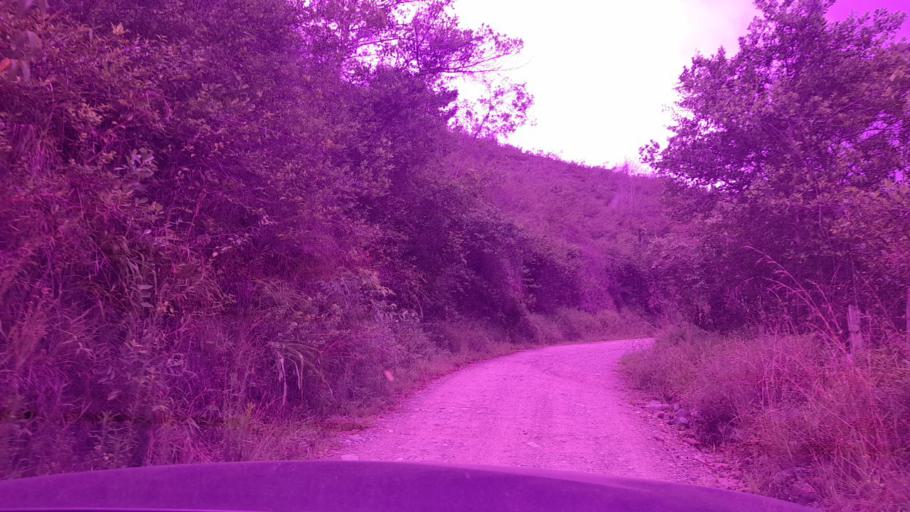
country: CO
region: Valle del Cauca
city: Andalucia
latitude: 4.1719
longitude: -76.1223
